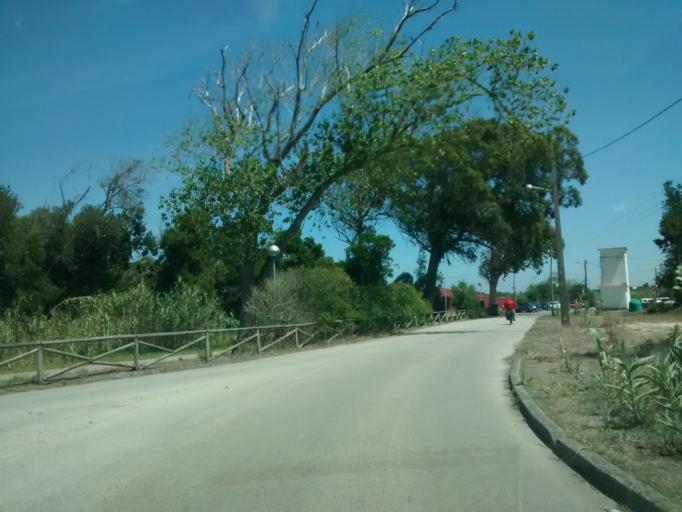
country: PT
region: Coimbra
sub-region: Mira
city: Mira
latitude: 40.4447
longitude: -8.7980
